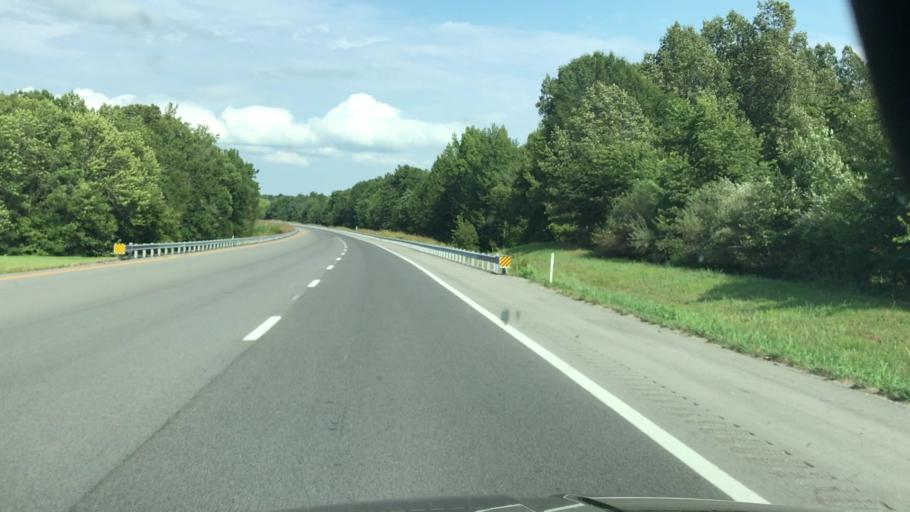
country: US
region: Kentucky
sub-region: Hopkins County
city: Nortonville
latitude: 37.2105
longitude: -87.4140
